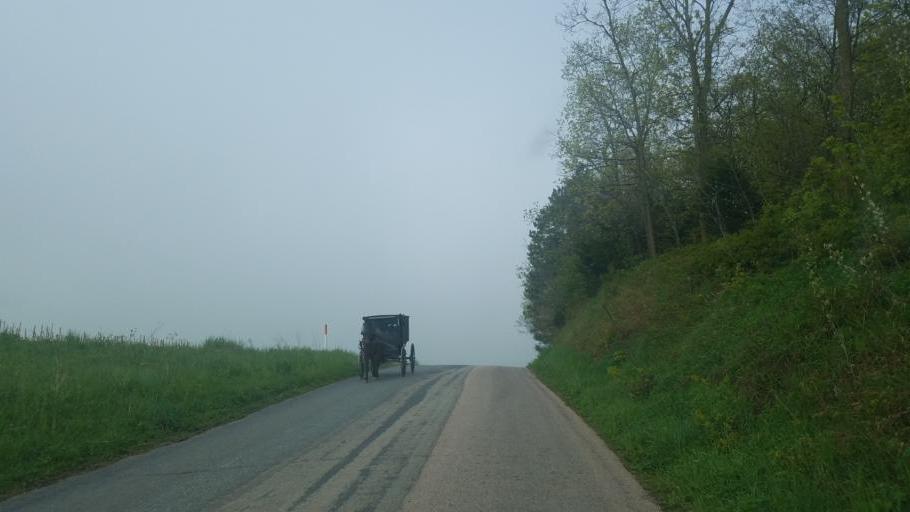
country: US
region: Wisconsin
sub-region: Vernon County
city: Hillsboro
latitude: 43.6186
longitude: -90.3954
